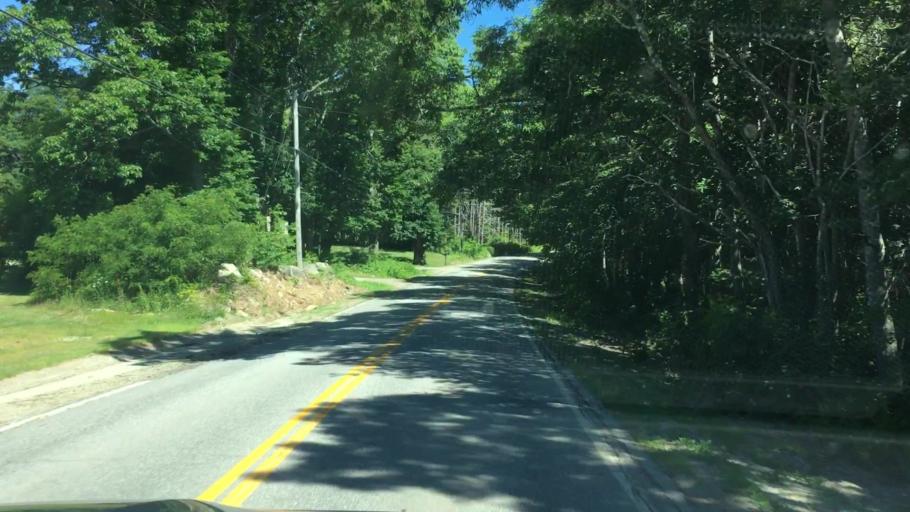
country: US
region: Maine
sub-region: Hancock County
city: Penobscot
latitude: 44.4328
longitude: -68.7140
